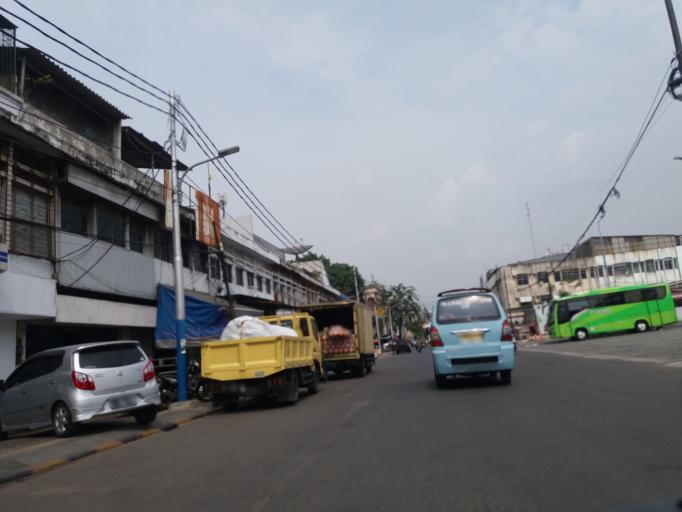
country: ID
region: Jakarta Raya
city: Jakarta
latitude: -6.1311
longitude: 106.8121
